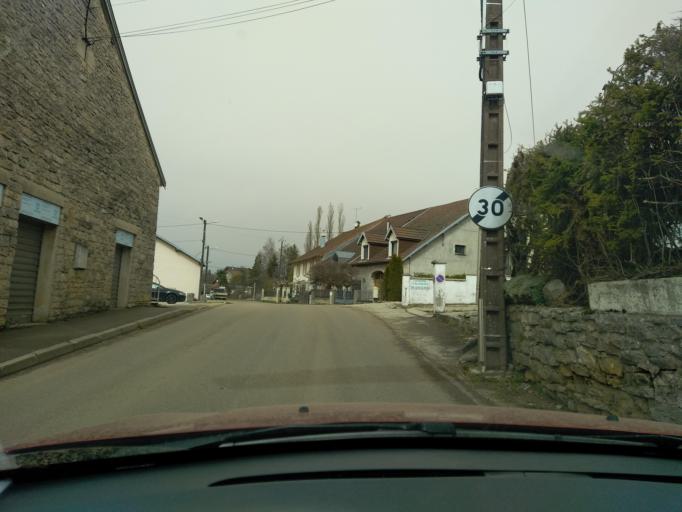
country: FR
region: Franche-Comte
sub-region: Departement du Jura
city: Clairvaux-les-Lacs
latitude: 46.6566
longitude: 5.7784
